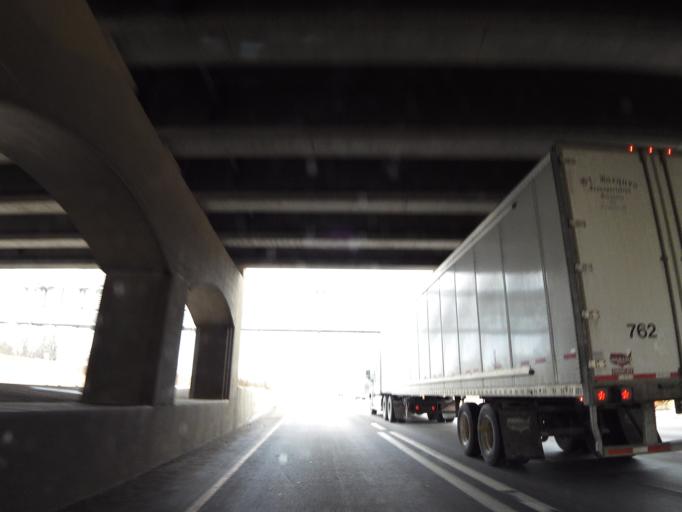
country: US
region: Minnesota
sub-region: Hennepin County
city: Richfield
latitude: 44.8654
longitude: -93.2988
